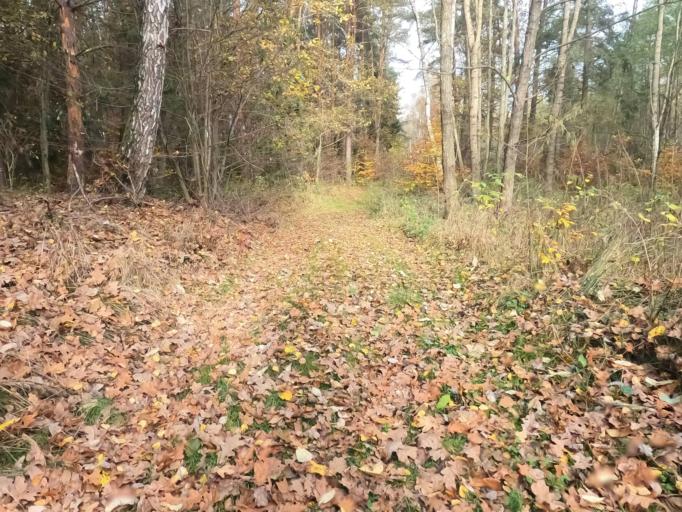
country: PL
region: Pomeranian Voivodeship
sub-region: Powiat starogardzki
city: Skarszewy
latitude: 54.0066
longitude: 18.4593
